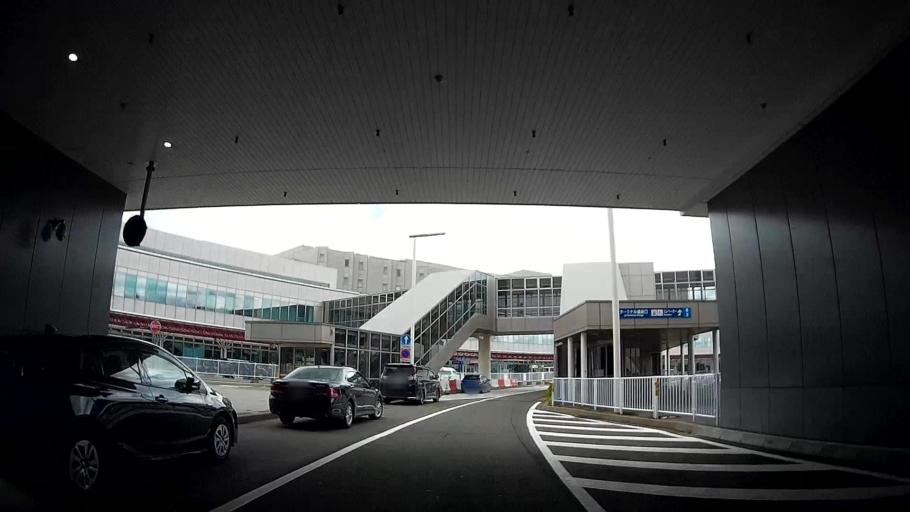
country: JP
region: Hokkaido
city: Chitose
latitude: 42.7868
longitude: 141.6807
